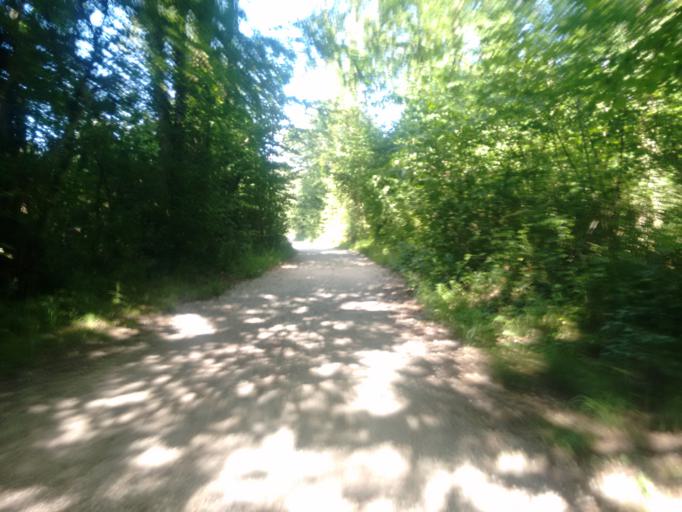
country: AT
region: Upper Austria
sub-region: Wels-Land
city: Thalheim bei Wels
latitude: 48.1453
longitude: 14.0138
